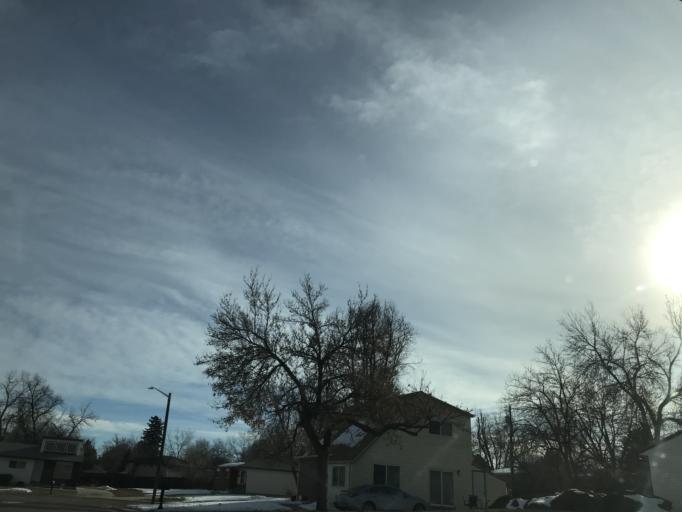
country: US
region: Colorado
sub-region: Arapahoe County
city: Littleton
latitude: 39.6010
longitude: -105.0139
